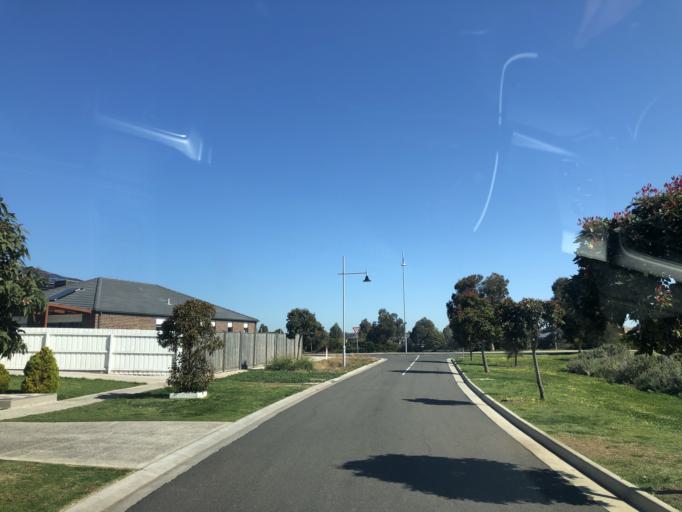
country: AU
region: Victoria
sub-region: Wyndham
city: Point Cook
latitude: -37.9074
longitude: 144.7288
